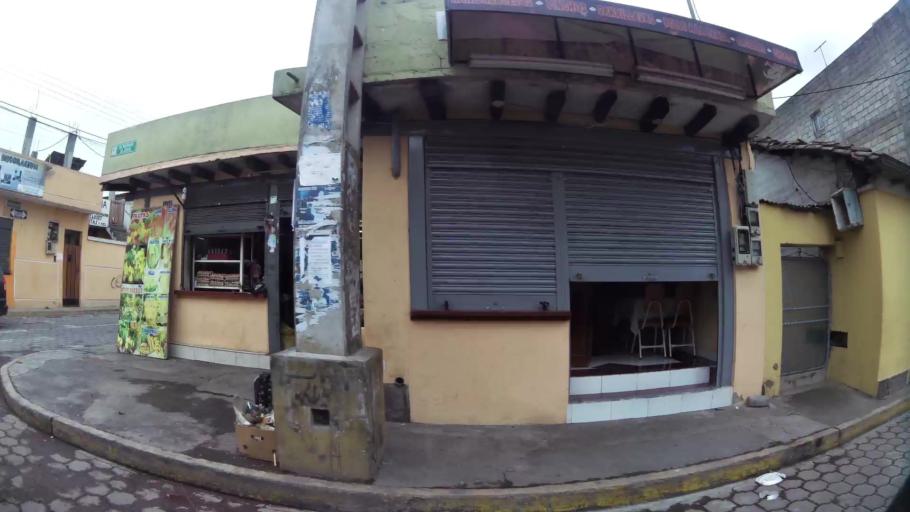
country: EC
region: Pichincha
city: Sangolqui
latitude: -0.3202
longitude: -78.4602
